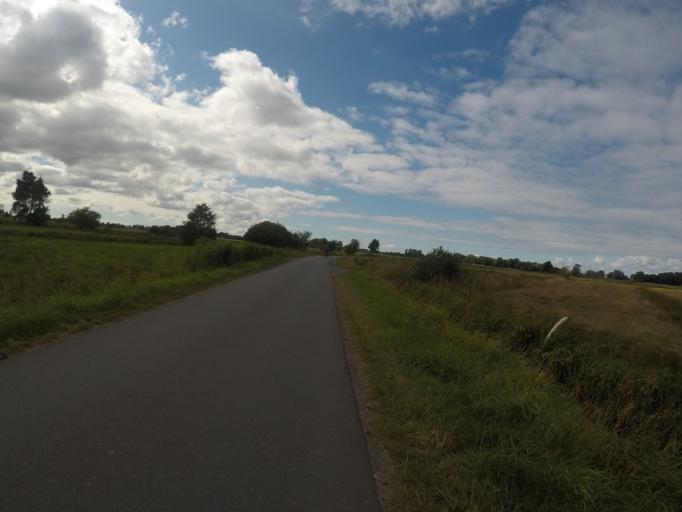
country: DE
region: Lower Saxony
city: Cadenberge
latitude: 53.7605
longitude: 9.0244
